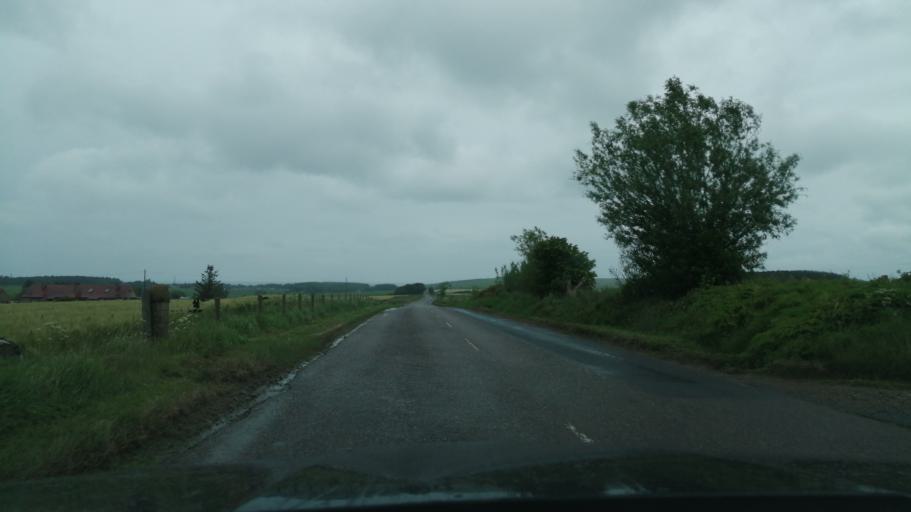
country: GB
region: Scotland
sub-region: Aberdeenshire
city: Portsoy
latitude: 57.6561
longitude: -2.7013
